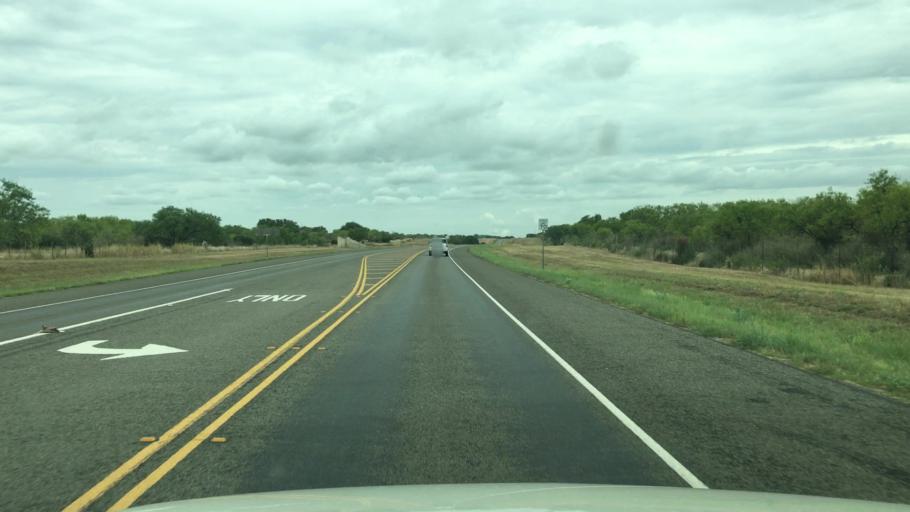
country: US
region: Texas
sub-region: Llano County
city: Kingsland
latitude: 30.5696
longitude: -98.4861
